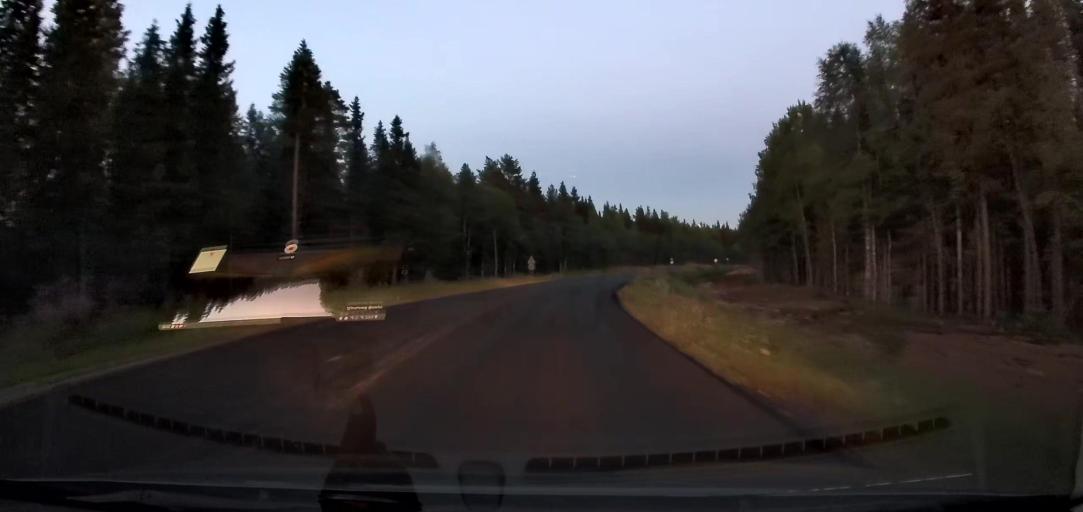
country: RU
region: Arkhangelskaya
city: Kholmogory
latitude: 64.3467
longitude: 41.3827
